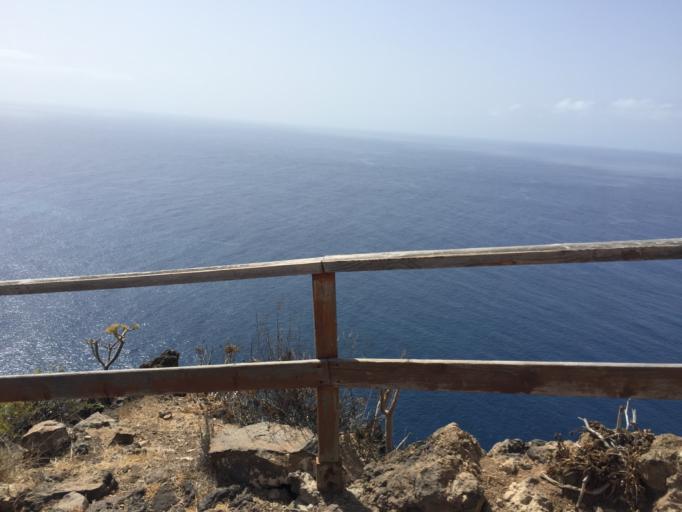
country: ES
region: Canary Islands
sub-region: Provincia de Santa Cruz de Tenerife
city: Tazacorte
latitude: 28.6535
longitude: -17.9495
